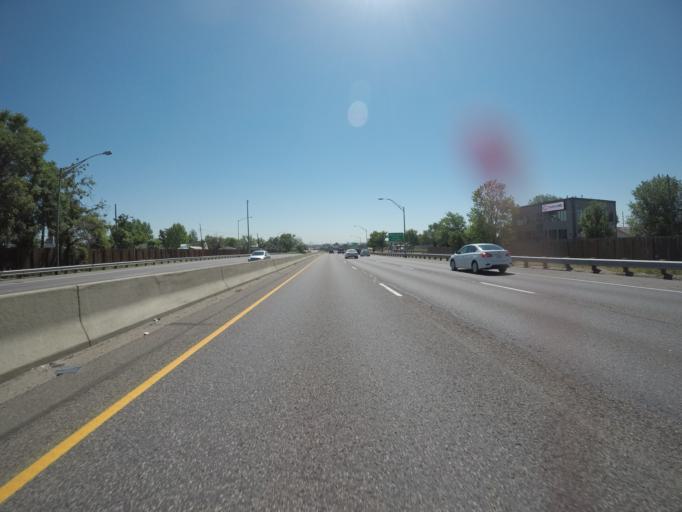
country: US
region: Colorado
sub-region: Adams County
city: Berkley
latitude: 39.7835
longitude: -105.0120
